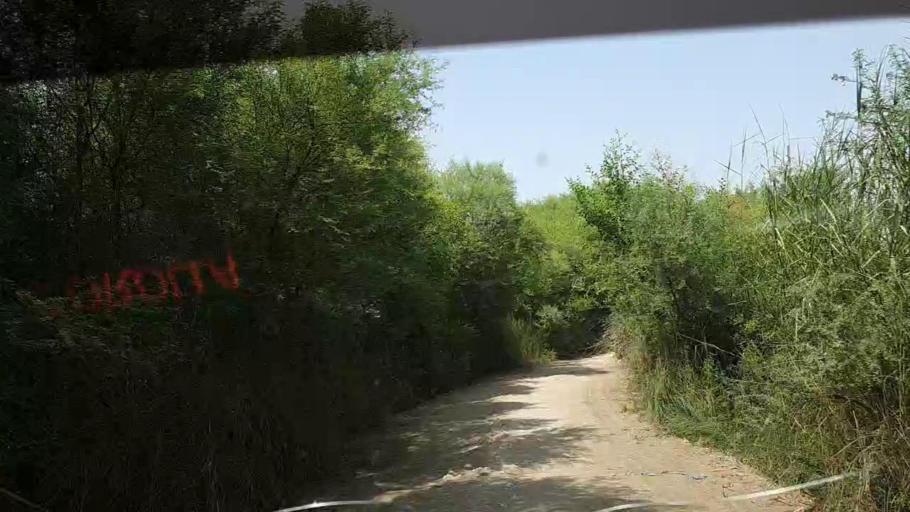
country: PK
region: Sindh
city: Ghotki
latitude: 28.1025
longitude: 69.3114
